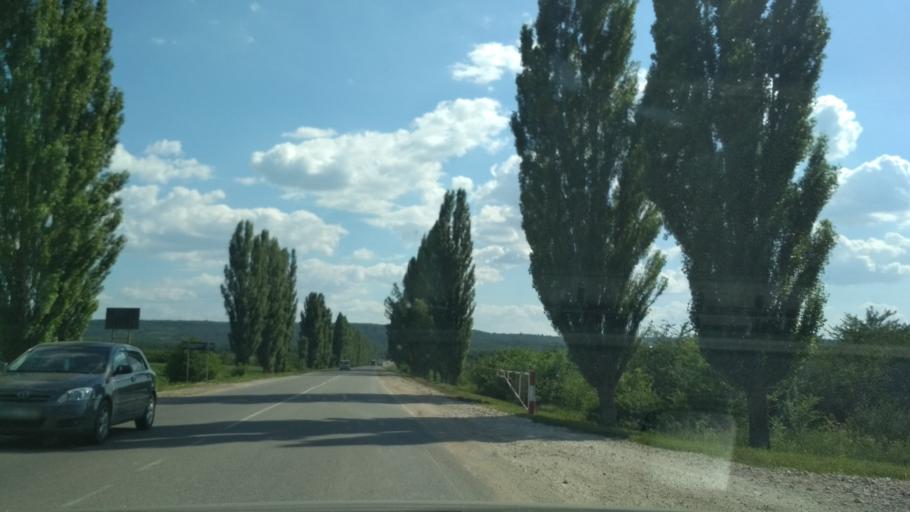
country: MD
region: Chisinau
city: Vadul lui Voda
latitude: 47.1010
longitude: 29.0983
